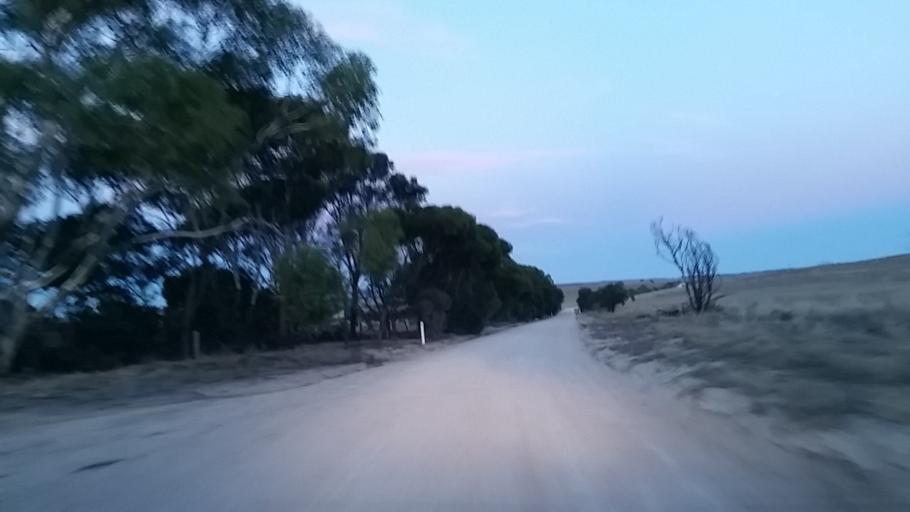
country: AU
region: South Australia
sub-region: Mount Barker
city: Callington
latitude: -35.1055
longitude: 139.0122
